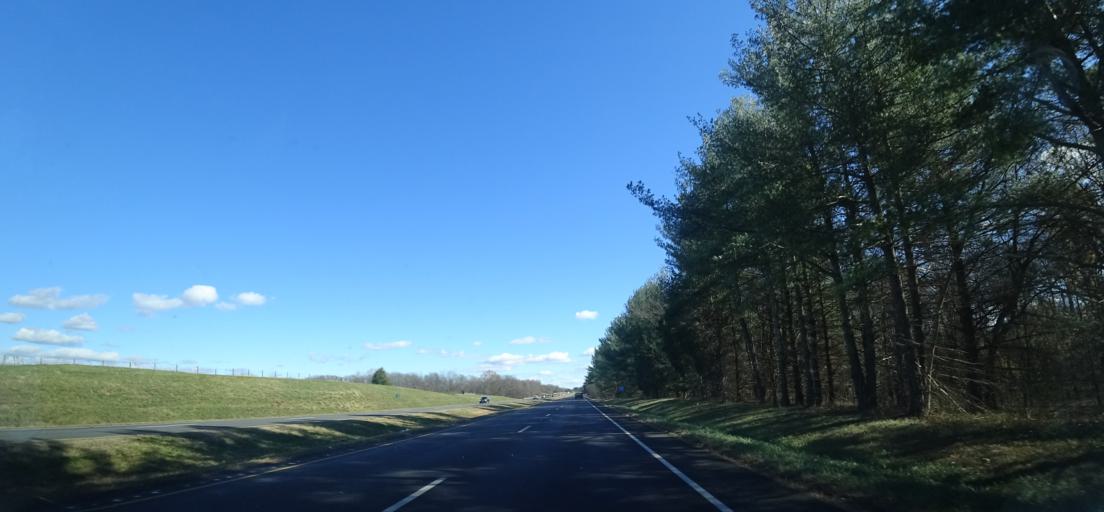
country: US
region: Virginia
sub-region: Culpeper County
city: Culpeper
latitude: 38.4999
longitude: -77.9166
